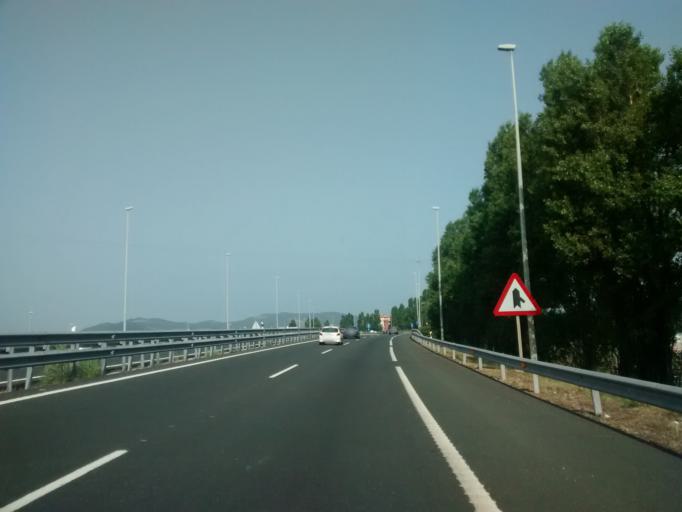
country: ES
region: Cantabria
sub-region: Provincia de Cantabria
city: Santa Cruz de Bezana
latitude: 43.4393
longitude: -3.8878
